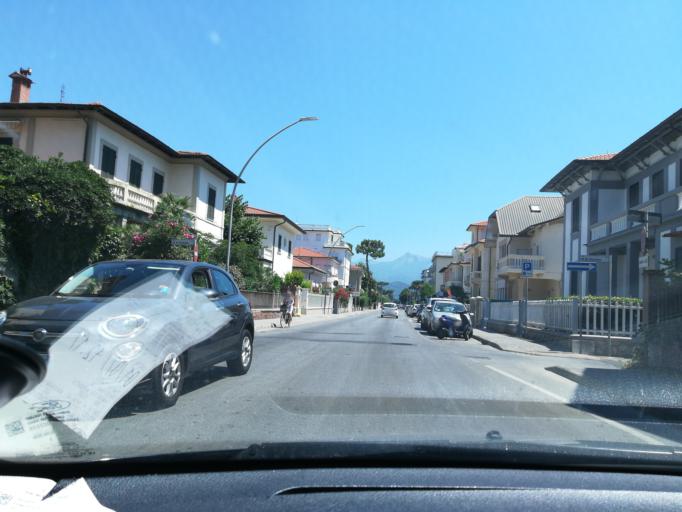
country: IT
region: Tuscany
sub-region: Provincia di Lucca
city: Camaiore
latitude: 43.8996
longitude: 10.2226
